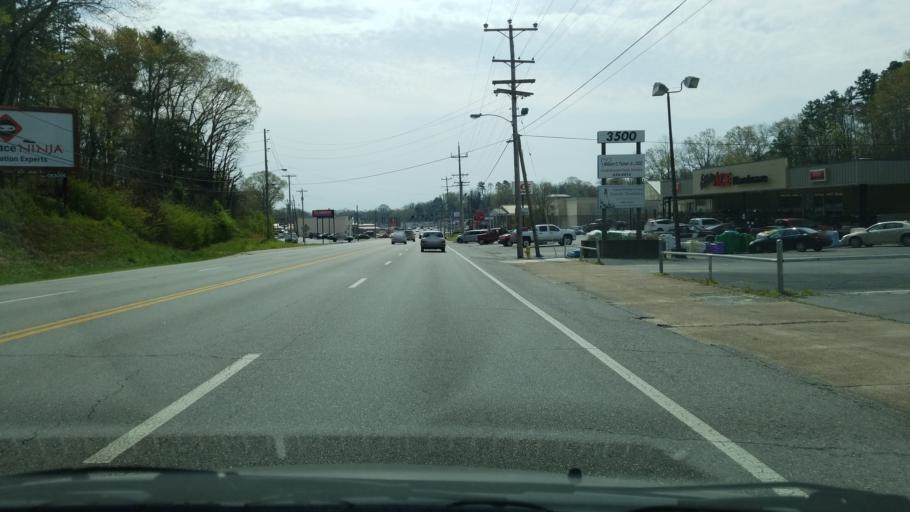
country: US
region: Tennessee
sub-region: Hamilton County
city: East Ridge
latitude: 35.0051
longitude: -85.2611
